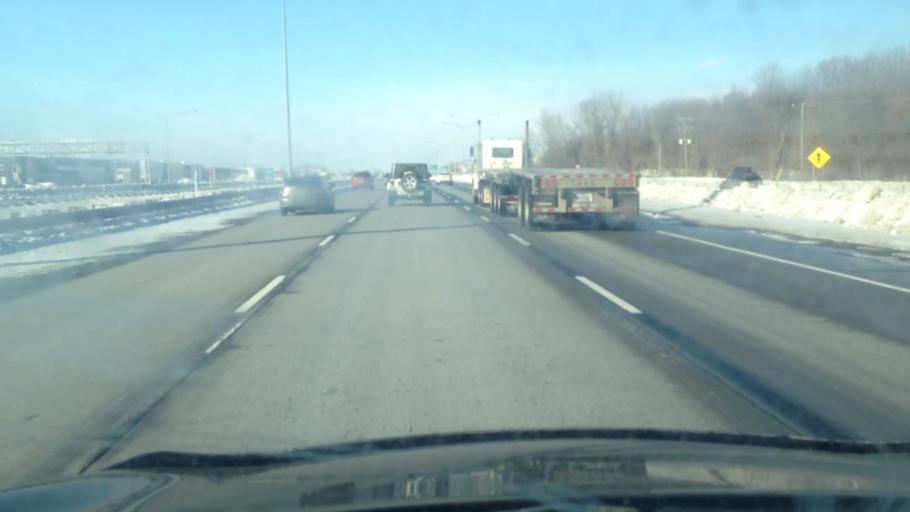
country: CA
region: Quebec
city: Dollard-Des Ormeaux
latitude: 45.5563
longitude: -73.8107
